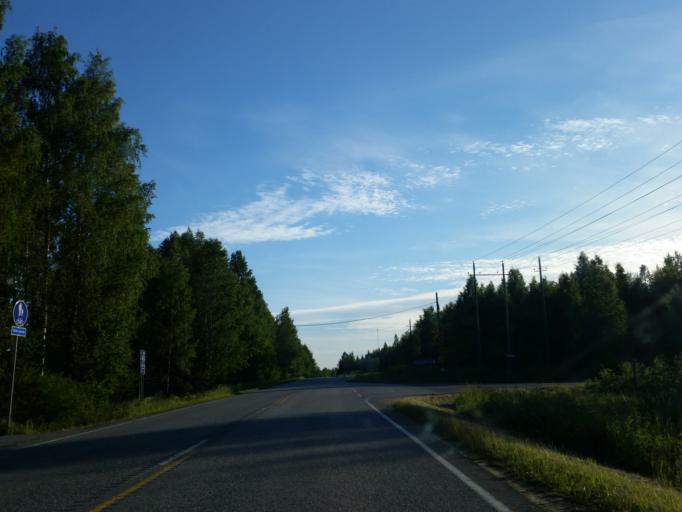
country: FI
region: Northern Savo
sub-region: Kuopio
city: Karttula
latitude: 62.9033
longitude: 26.9553
